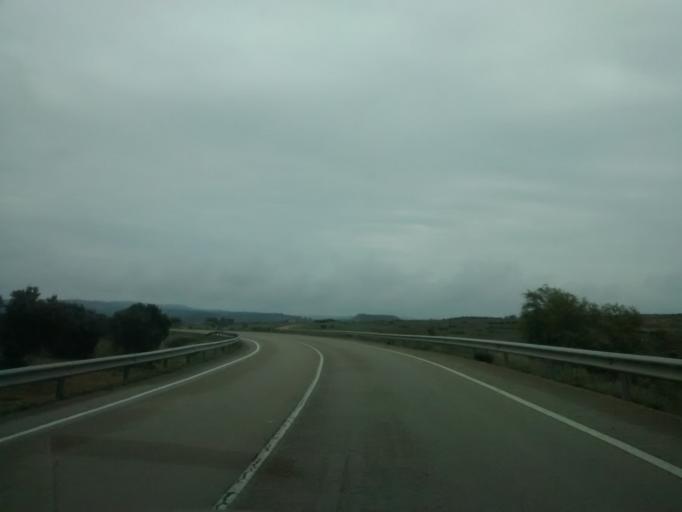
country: ES
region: Aragon
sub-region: Provincia de Zaragoza
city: Caspe
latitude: 41.2142
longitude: -0.0073
